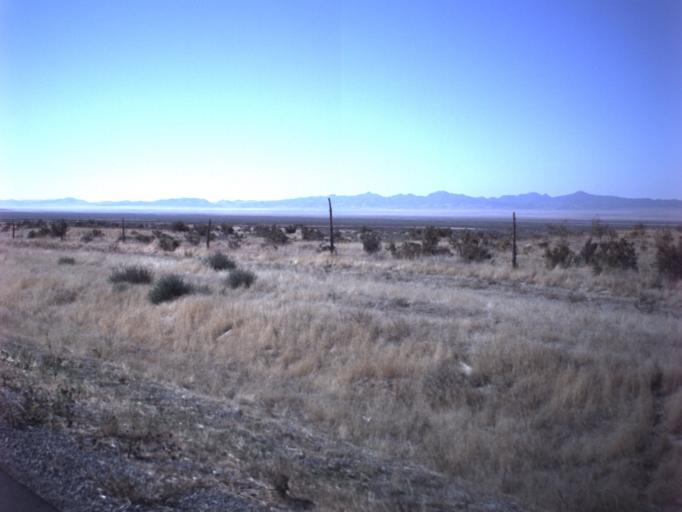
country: US
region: Utah
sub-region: Tooele County
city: Grantsville
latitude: 40.5082
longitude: -112.7479
